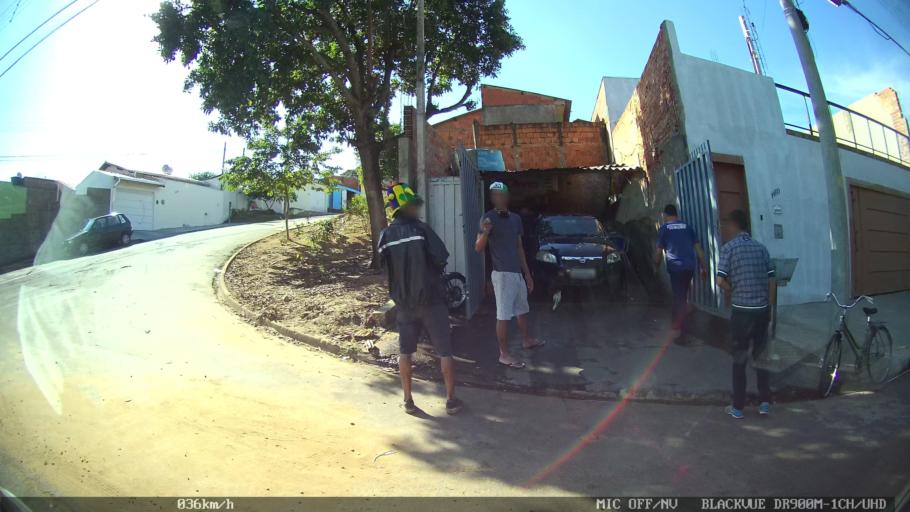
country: BR
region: Sao Paulo
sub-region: Franca
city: Franca
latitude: -20.4914
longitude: -47.4183
